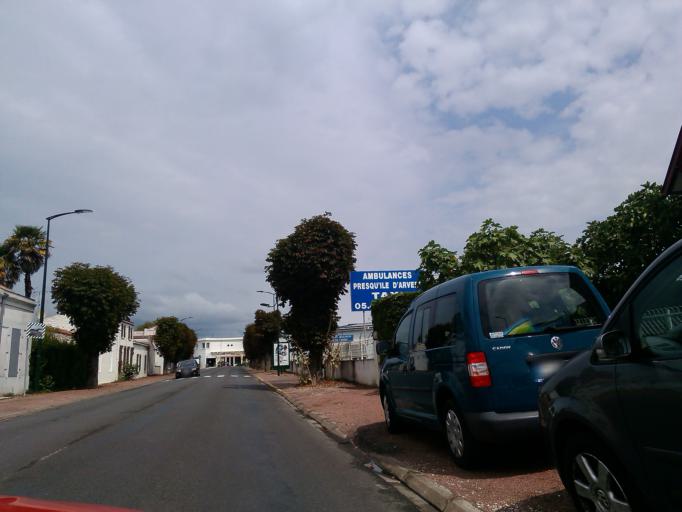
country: FR
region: Poitou-Charentes
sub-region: Departement de la Charente-Maritime
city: La Tremblade
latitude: 45.7629
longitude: -1.1419
